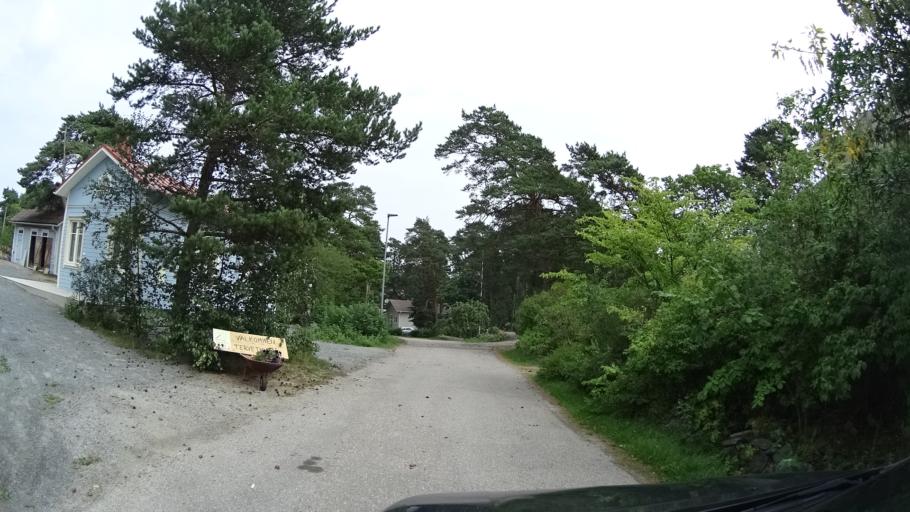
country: FI
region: Uusimaa
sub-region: Raaseporin
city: Hanko
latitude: 59.8270
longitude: 22.9815
